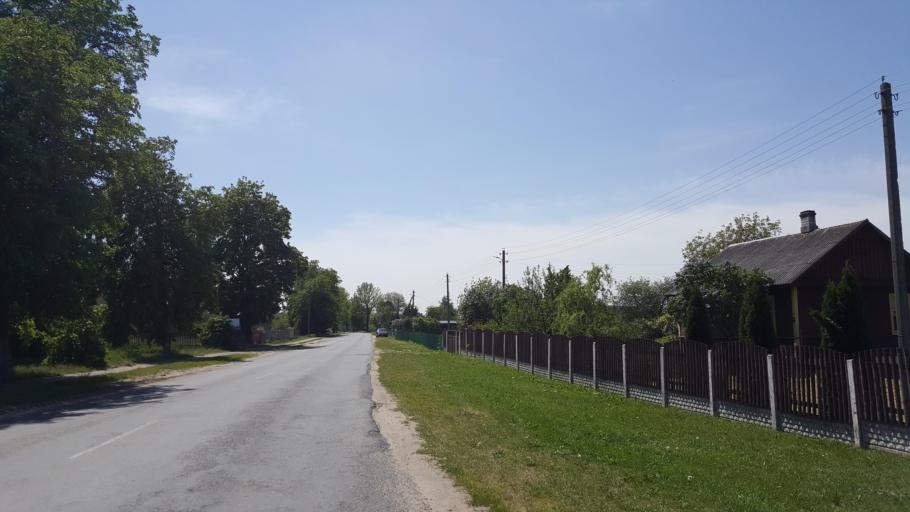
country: BY
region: Brest
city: Charnawchytsy
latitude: 52.2130
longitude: 23.7389
